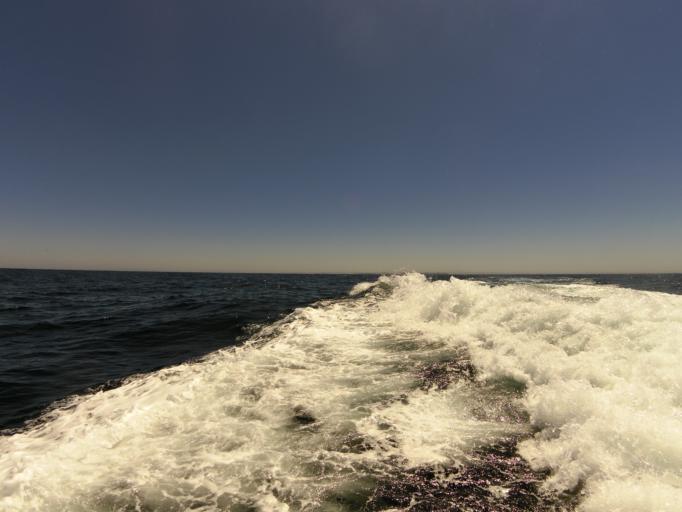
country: PT
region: Leiria
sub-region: Peniche
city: Peniche
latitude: 39.3906
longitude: -9.4728
